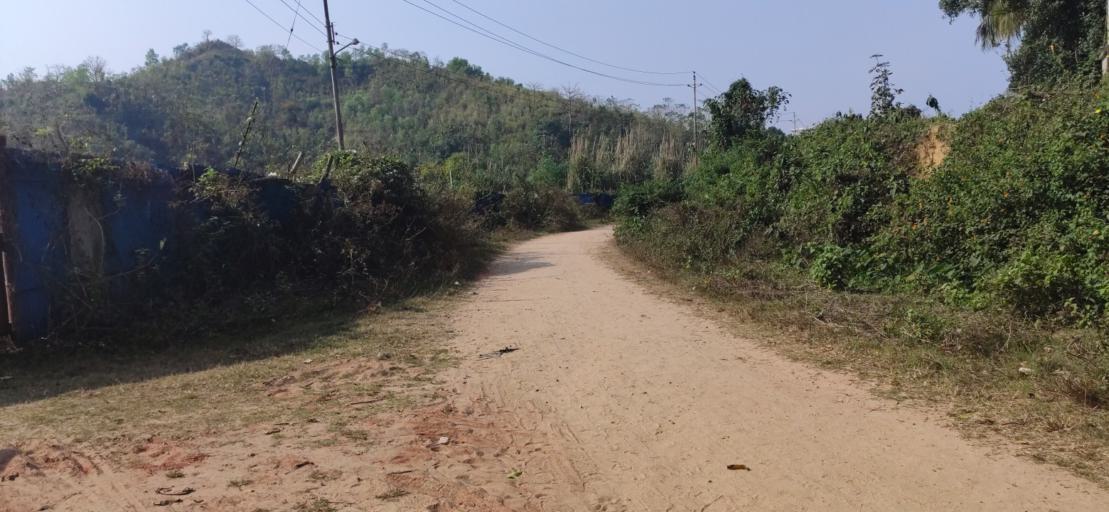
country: BD
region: Chittagong
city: Chittagong
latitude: 22.4740
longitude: 91.7846
